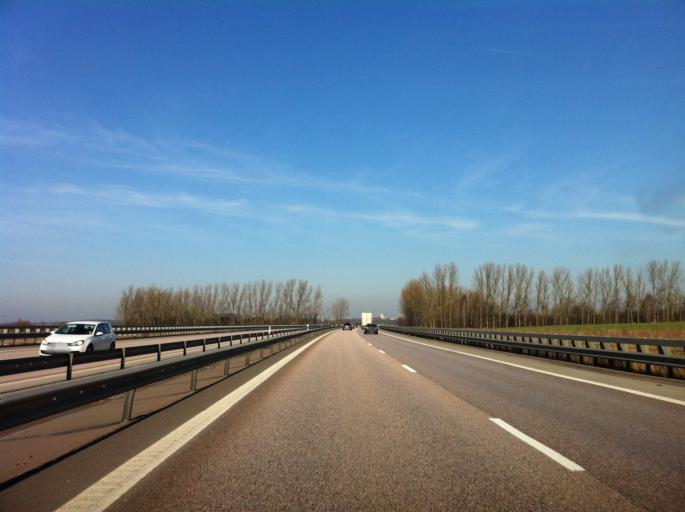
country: SE
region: Skane
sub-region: Helsingborg
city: Gantofta
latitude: 55.9853
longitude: 12.7822
